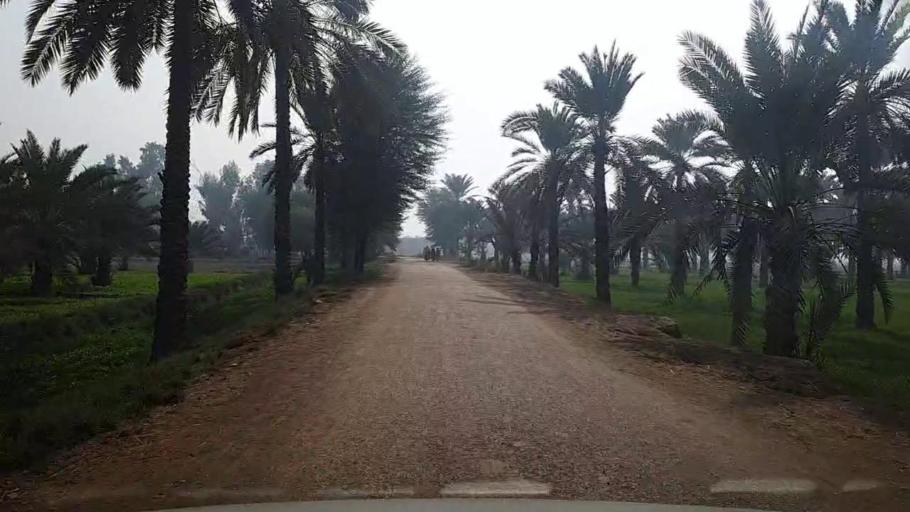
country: PK
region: Sindh
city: Setharja Old
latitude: 27.1573
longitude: 68.4628
